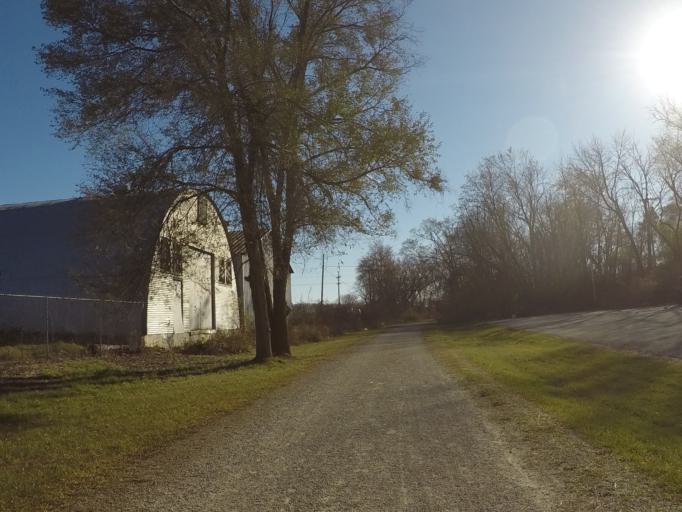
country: US
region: Wisconsin
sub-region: Dane County
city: Deerfield
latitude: 43.0551
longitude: -89.0729
